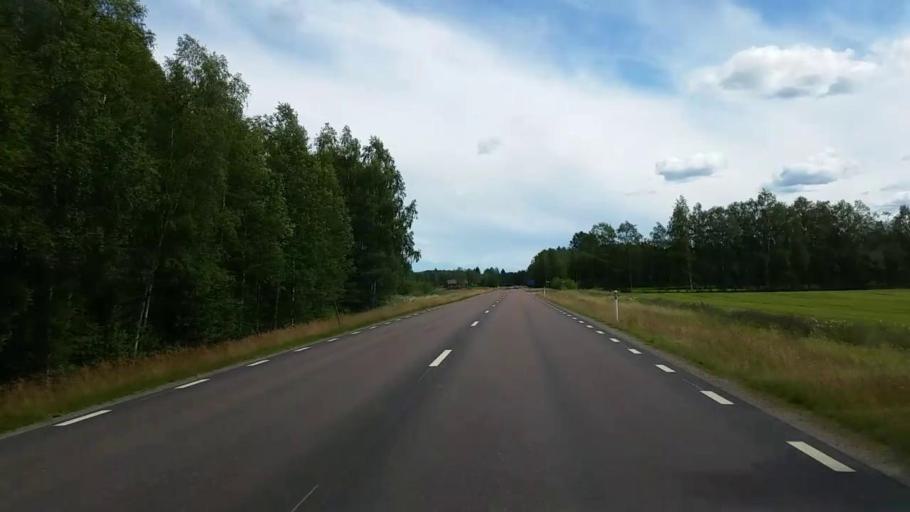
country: SE
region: Gaevleborg
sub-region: Ovanakers Kommun
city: Edsbyn
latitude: 61.3655
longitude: 15.8812
